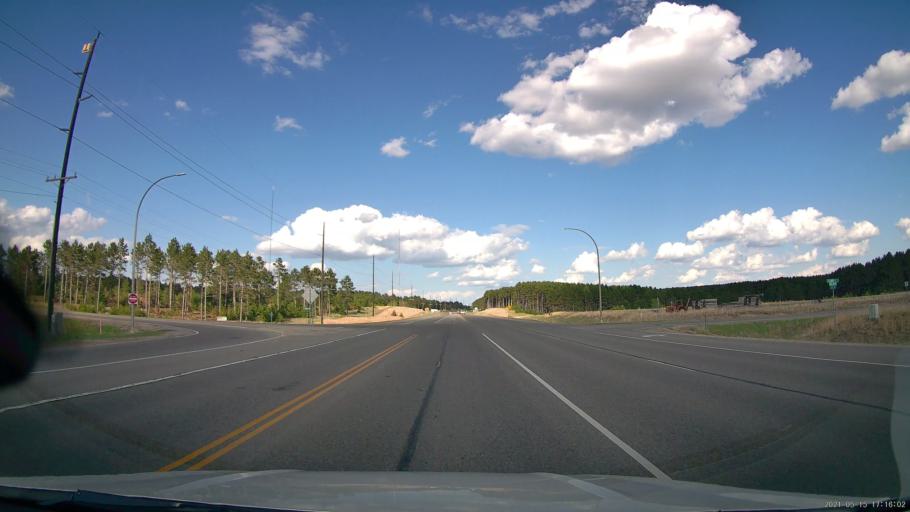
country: US
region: Minnesota
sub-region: Hubbard County
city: Park Rapids
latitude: 46.9251
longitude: -95.0158
